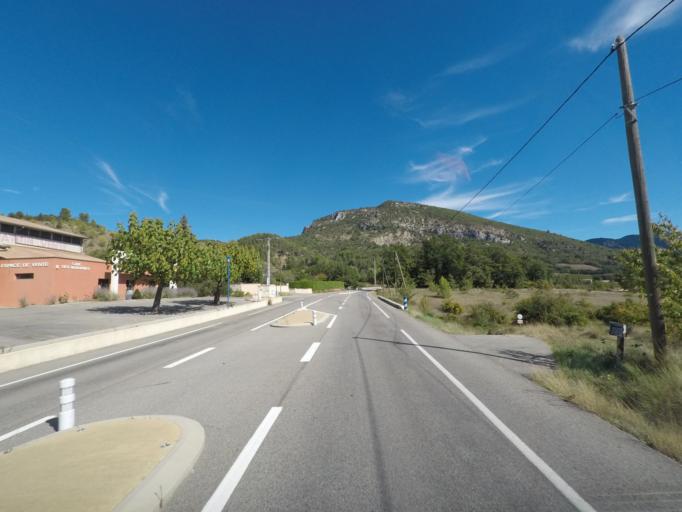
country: FR
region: Rhone-Alpes
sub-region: Departement de la Drome
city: Nyons
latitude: 44.3910
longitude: 5.2040
